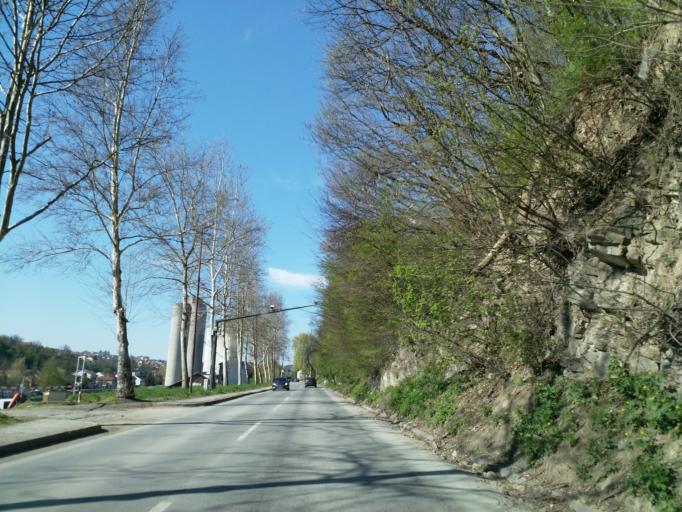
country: RS
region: Central Serbia
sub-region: Kolubarski Okrug
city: Valjevo
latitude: 44.2645
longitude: 19.8782
